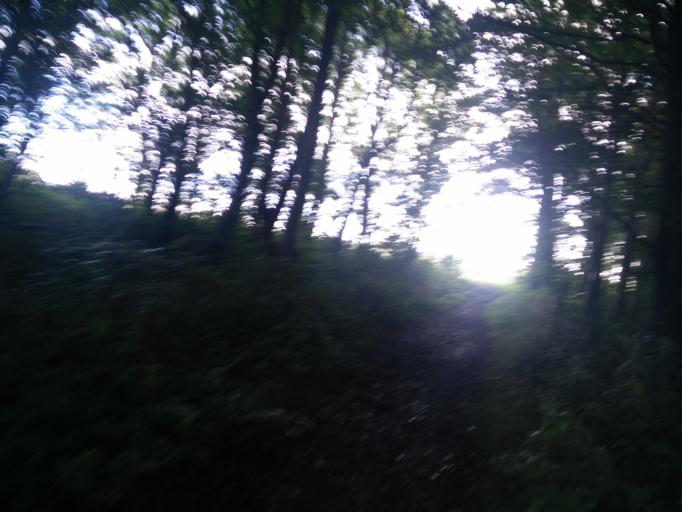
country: GB
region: England
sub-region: County Durham
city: Crook
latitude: 54.7230
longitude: -1.7645
